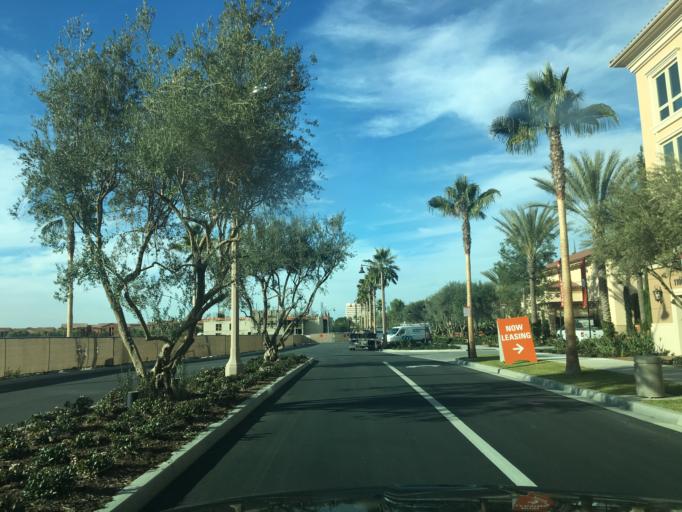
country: US
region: California
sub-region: Orange County
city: Laguna Woods
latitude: 33.6399
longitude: -117.7459
